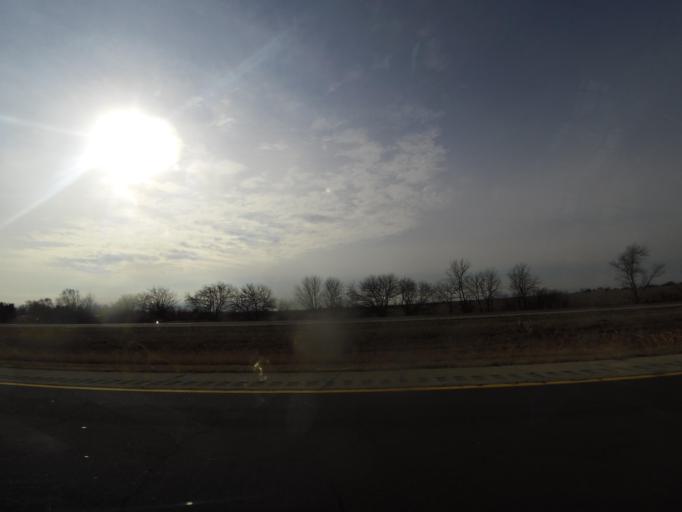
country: US
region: Illinois
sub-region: Macon County
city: Decatur
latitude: 39.7873
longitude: -88.9835
